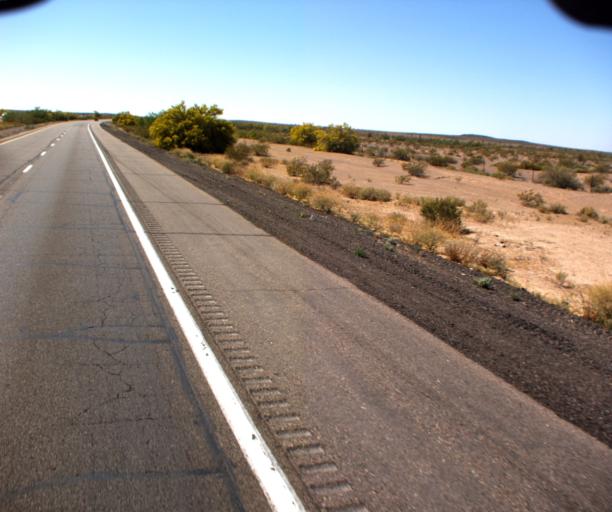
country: US
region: Arizona
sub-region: Maricopa County
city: Gila Bend
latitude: 32.8941
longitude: -113.0371
